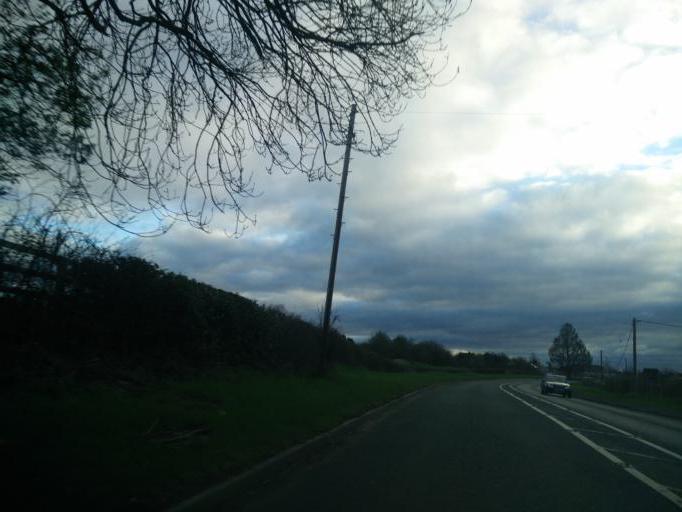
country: GB
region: England
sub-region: County Durham
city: Ushaw Moor
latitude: 54.7463
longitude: -1.6330
